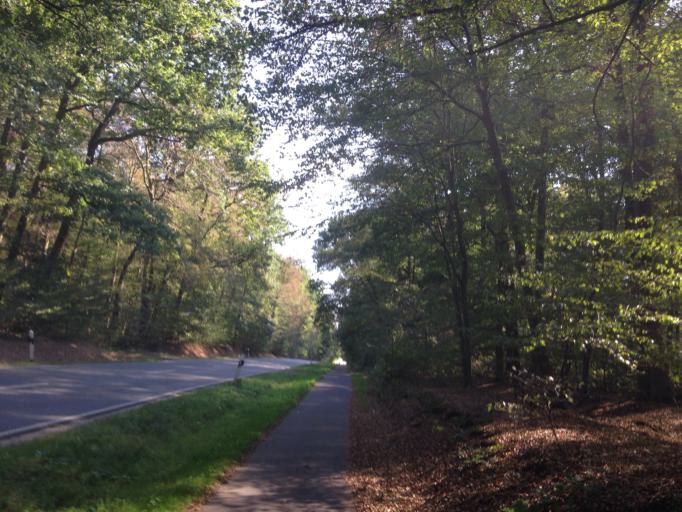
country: DE
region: Hesse
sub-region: Regierungsbezirk Giessen
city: Giessen
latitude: 50.5525
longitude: 8.6995
